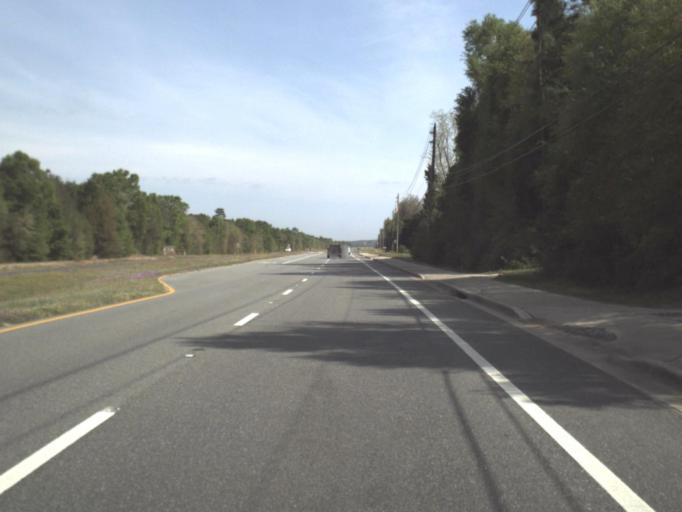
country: US
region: Florida
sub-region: Santa Rosa County
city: East Milton
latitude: 30.6110
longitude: -86.9565
